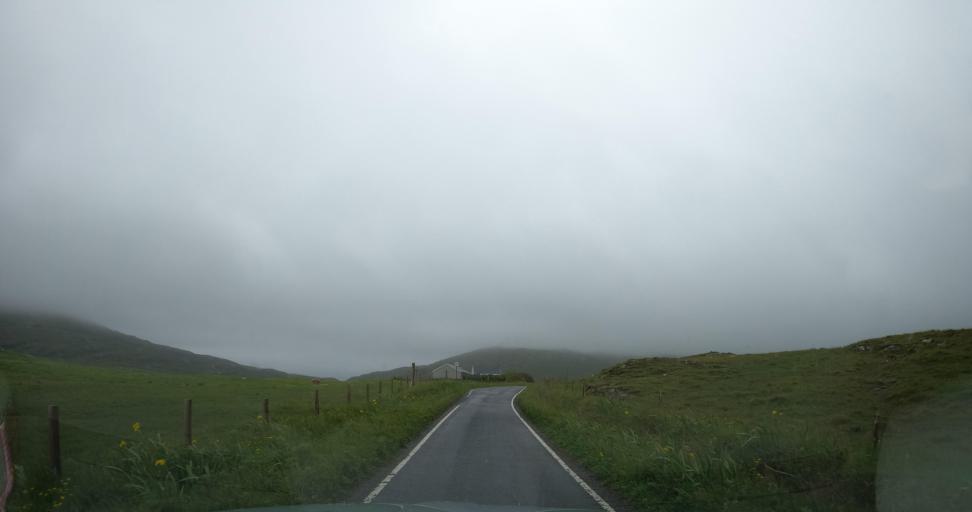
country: GB
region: Scotland
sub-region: Eilean Siar
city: Barra
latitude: 57.0021
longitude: -7.4887
